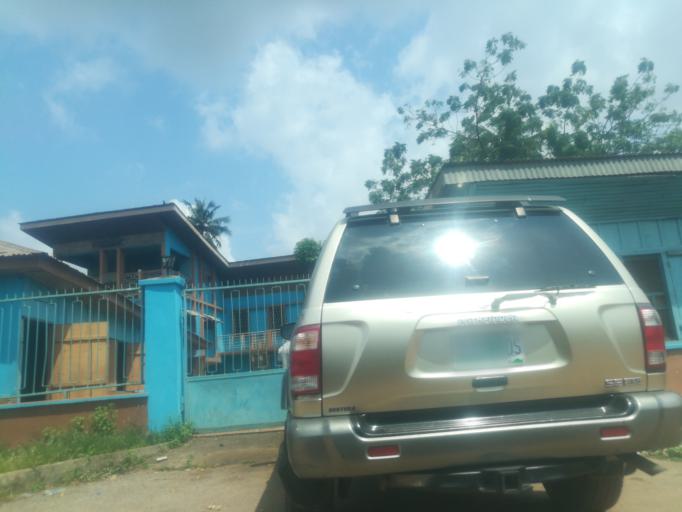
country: NG
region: Oyo
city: Ibadan
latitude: 7.3653
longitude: 3.8769
